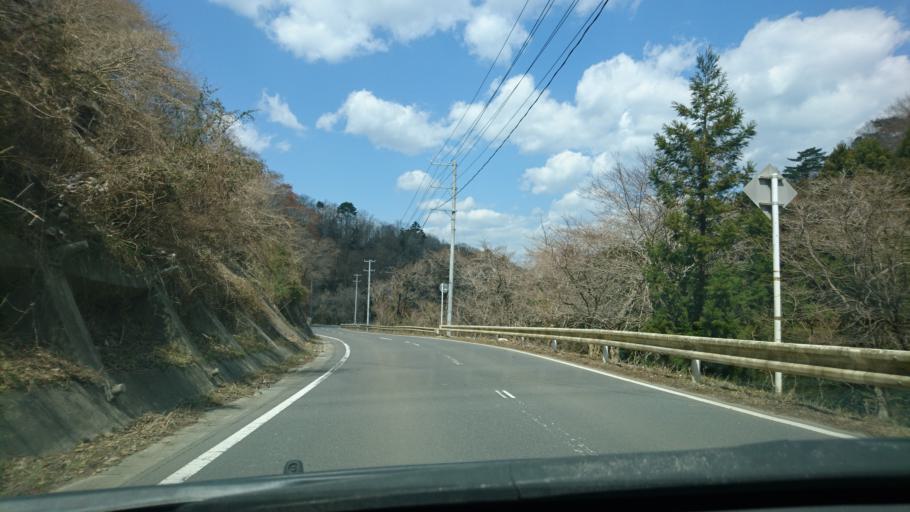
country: JP
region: Miyagi
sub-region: Oshika Gun
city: Onagawa Cho
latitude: 38.4567
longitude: 141.4865
